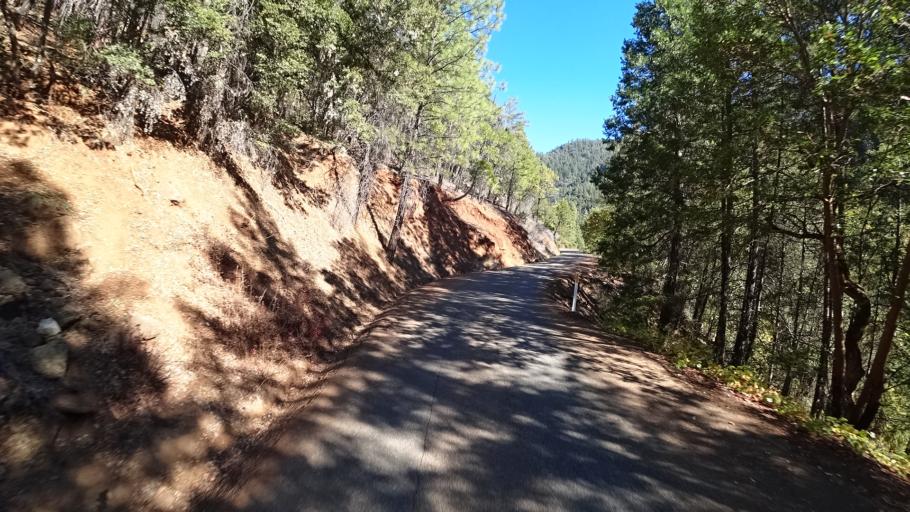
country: US
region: California
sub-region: Siskiyou County
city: Happy Camp
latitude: 41.2999
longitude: -123.2252
